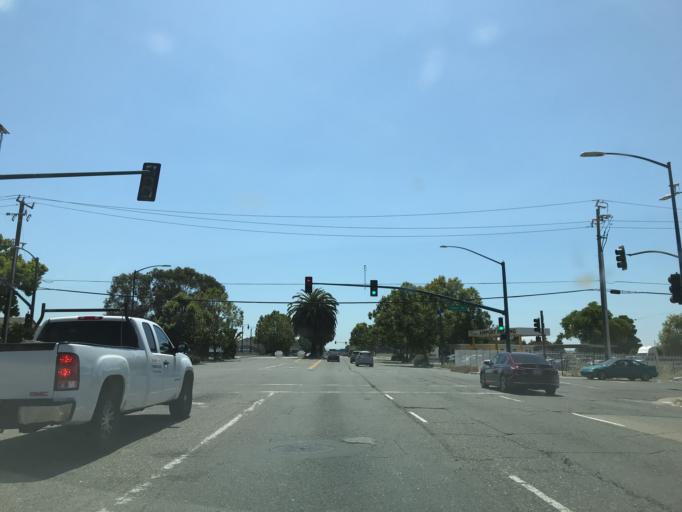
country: US
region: California
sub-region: Alameda County
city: San Leandro
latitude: 37.7306
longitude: -122.1911
